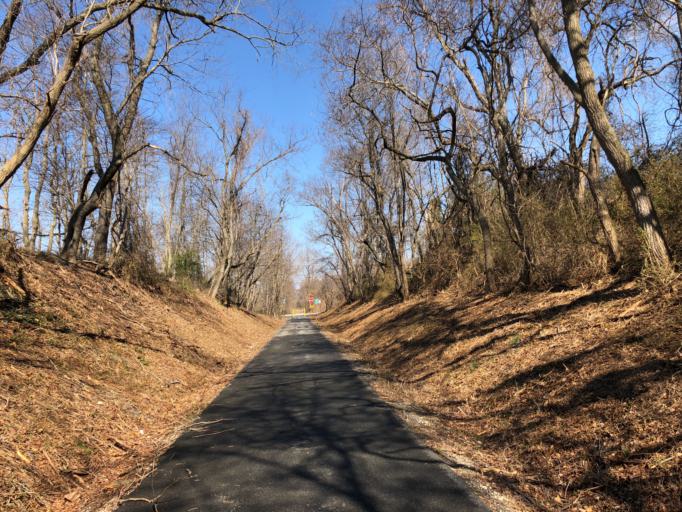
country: US
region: Maryland
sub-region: Kent County
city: Chestertown
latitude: 39.2207
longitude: -76.0728
